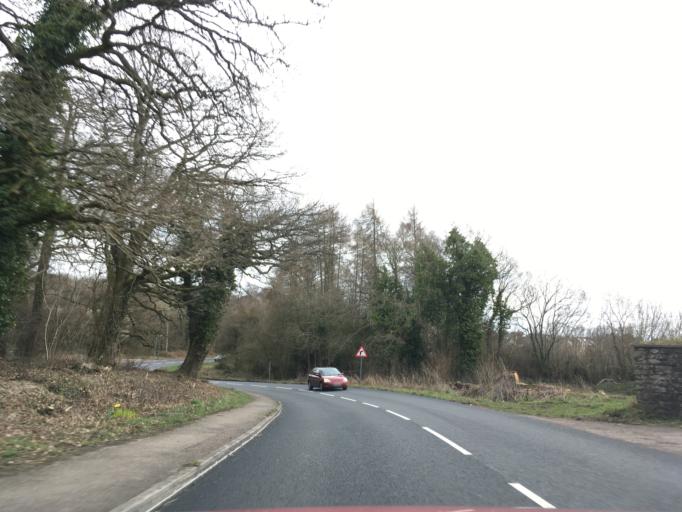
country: GB
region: England
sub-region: Gloucestershire
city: Coleford
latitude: 51.8067
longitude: -2.6075
